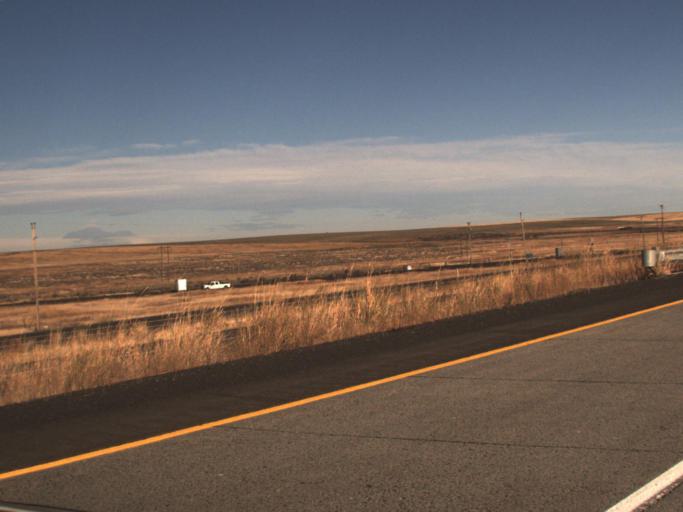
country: US
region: Washington
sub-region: Adams County
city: Ritzville
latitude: 47.1011
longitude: -118.4080
